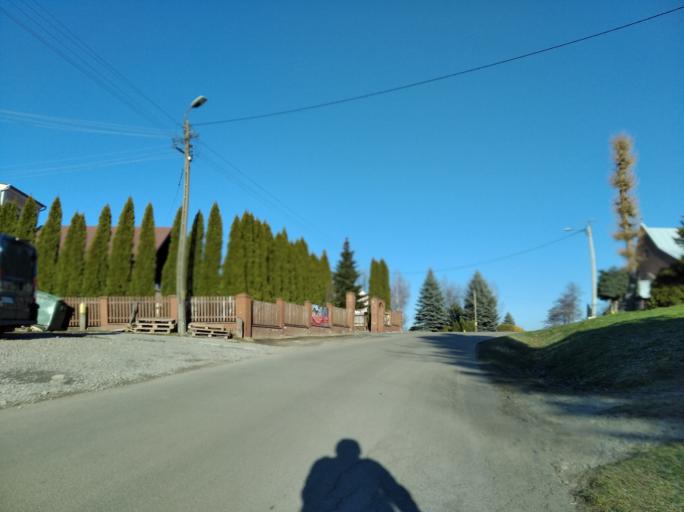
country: PL
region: Subcarpathian Voivodeship
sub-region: Powiat strzyzowski
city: Wysoka Strzyzowska
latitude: 49.8428
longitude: 21.7720
